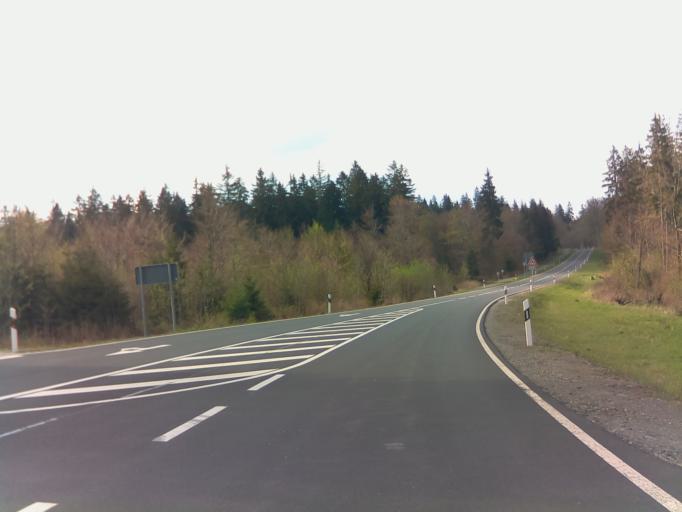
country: DE
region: Bavaria
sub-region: Upper Franconia
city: Ludwigsstadt
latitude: 50.4511
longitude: 11.3520
